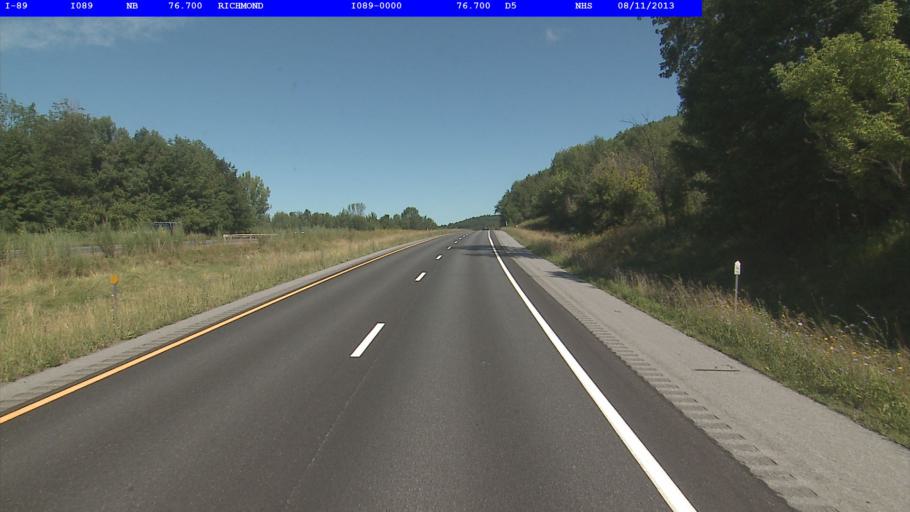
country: US
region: Vermont
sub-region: Chittenden County
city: Williston
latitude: 44.4064
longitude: -72.9895
